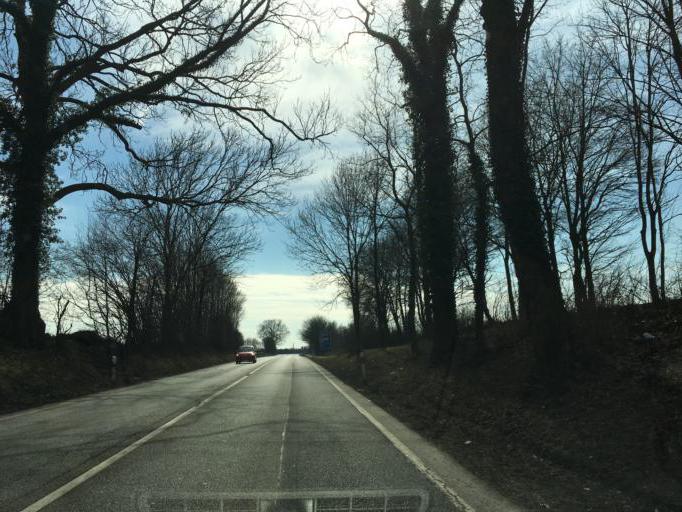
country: DE
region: Schleswig-Holstein
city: Hogersdorf
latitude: 53.9274
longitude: 10.2788
